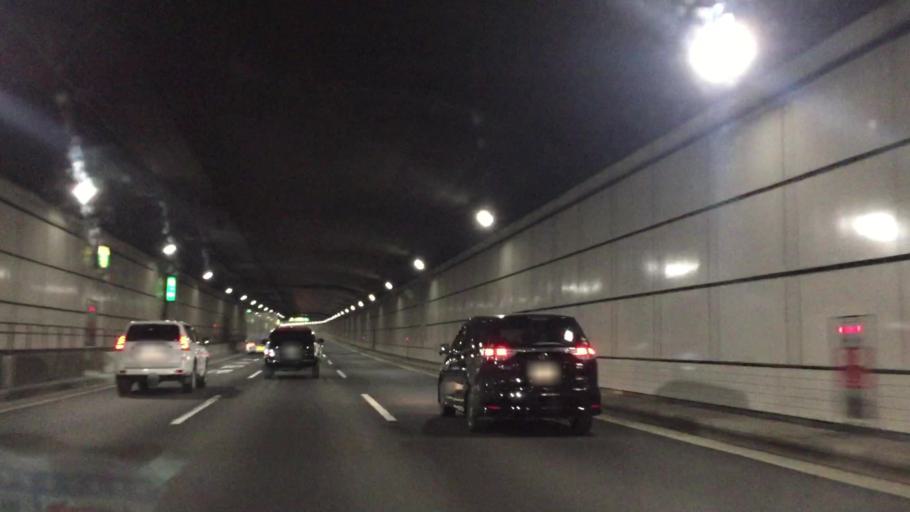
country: JP
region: Kanagawa
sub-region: Kawasaki-shi
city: Kawasaki
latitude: 35.5142
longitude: 139.7843
